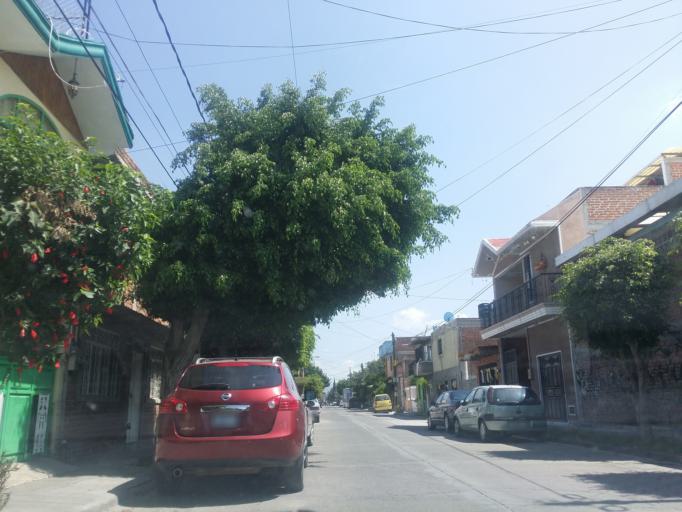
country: MX
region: Guanajuato
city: Leon
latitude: 21.1433
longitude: -101.6720
